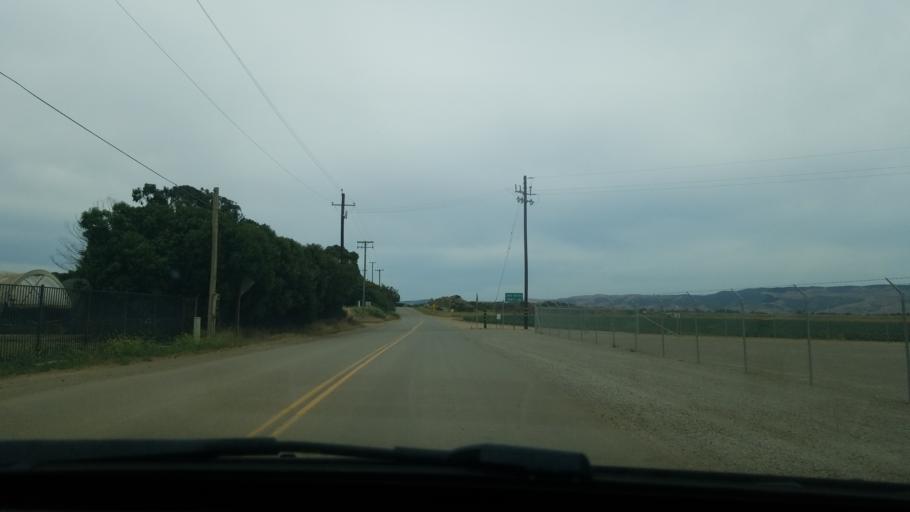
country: US
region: California
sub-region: Santa Barbara County
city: Guadalupe
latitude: 34.9898
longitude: -120.5139
